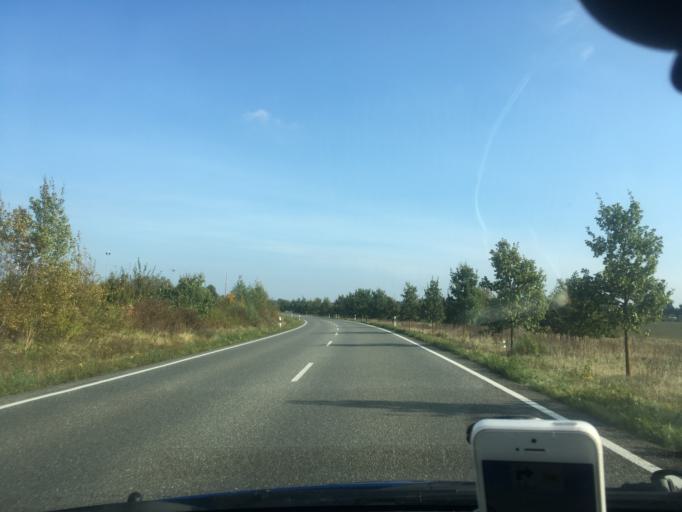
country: DE
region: Mecklenburg-Vorpommern
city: Klein Rogahn
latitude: 53.5612
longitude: 11.3567
